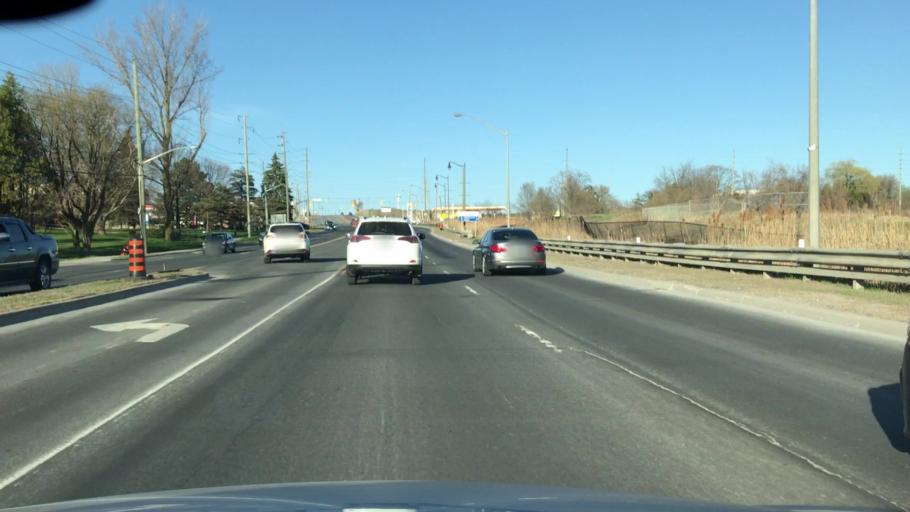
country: CA
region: Ontario
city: Newmarket
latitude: 44.0100
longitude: -79.4221
